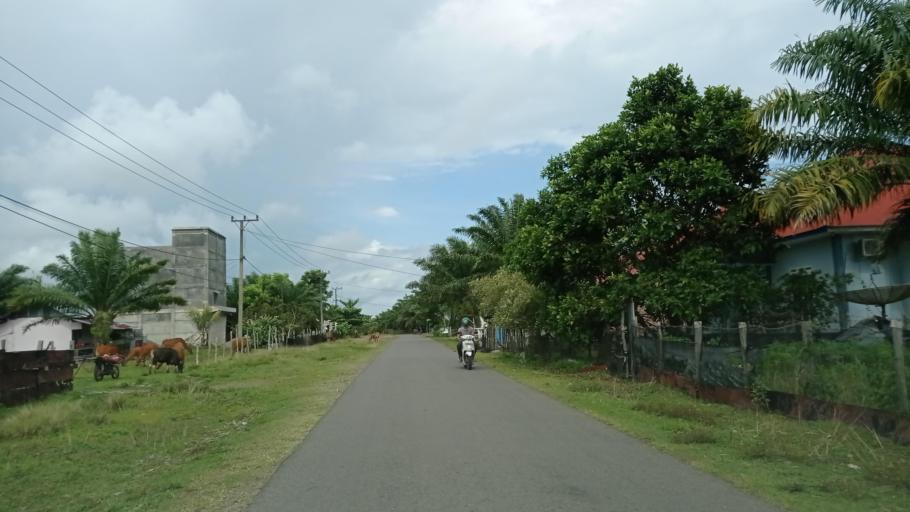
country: ID
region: Bengkulu
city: Ipuh
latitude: -2.5675
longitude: 101.1156
